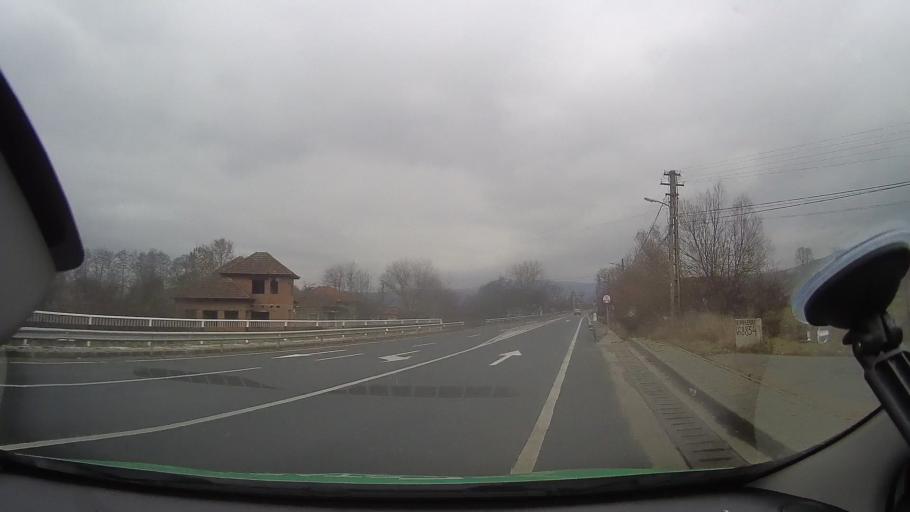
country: RO
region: Hunedoara
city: Vata de Jos
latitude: 46.1898
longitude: 22.6193
